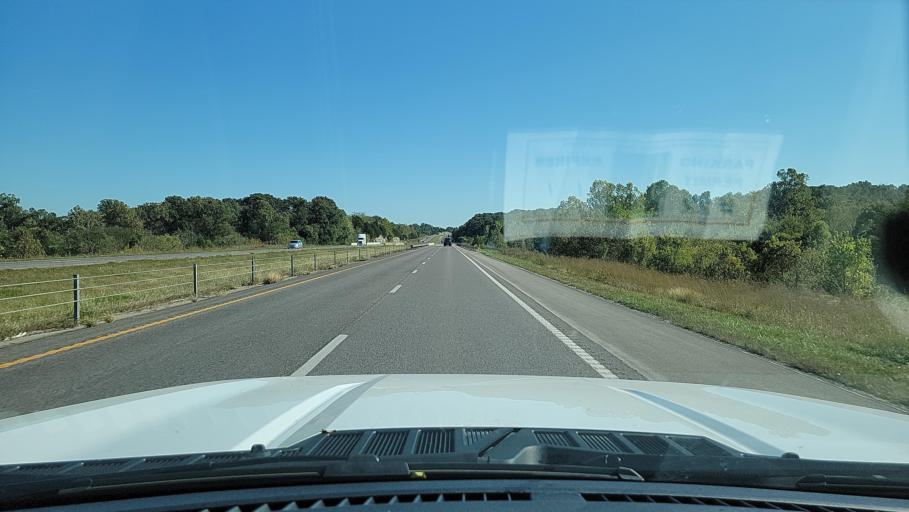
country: US
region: Missouri
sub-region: Sainte Genevieve County
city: Sainte Genevieve
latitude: 37.9958
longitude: -90.2108
